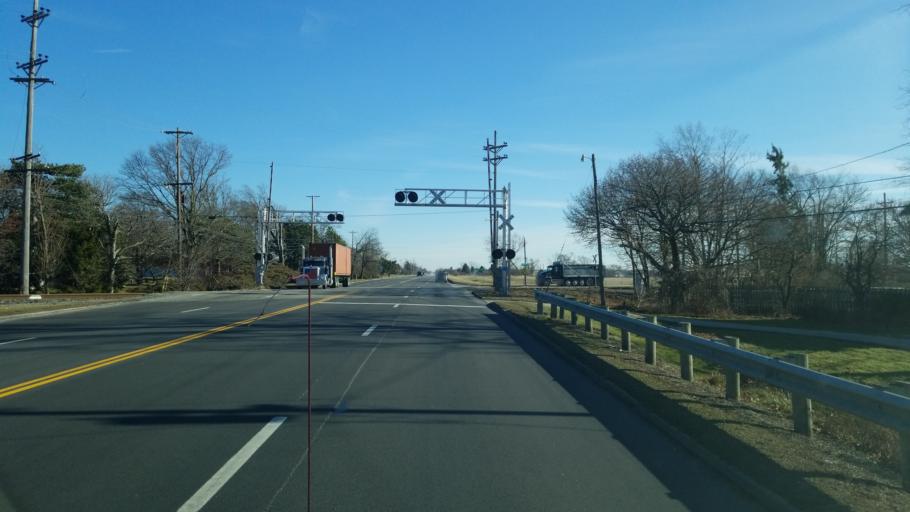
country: US
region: Ohio
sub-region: Sandusky County
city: Woodville
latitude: 41.4485
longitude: -83.3582
